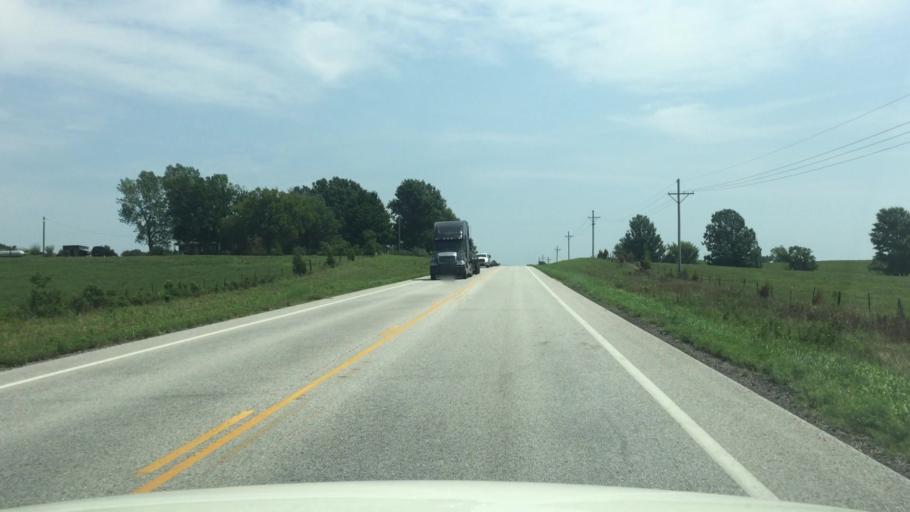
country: US
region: Kansas
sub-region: Cherokee County
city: Columbus
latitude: 37.1780
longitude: -94.7907
